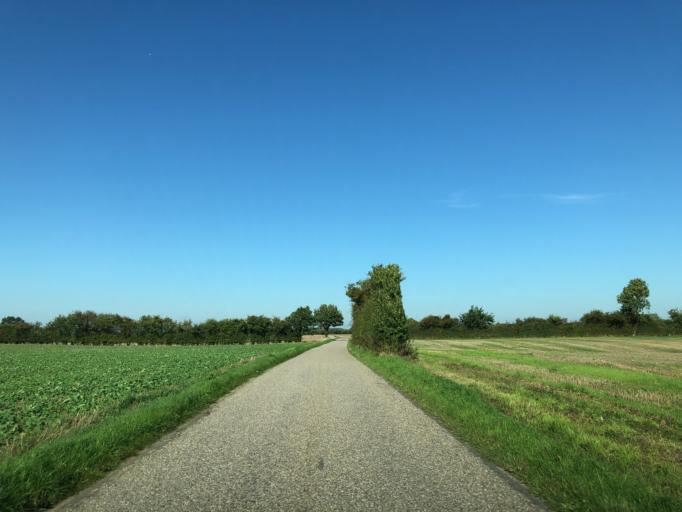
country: DK
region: South Denmark
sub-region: Sonderborg Kommune
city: Dybbol
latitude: 54.9404
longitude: 9.7319
